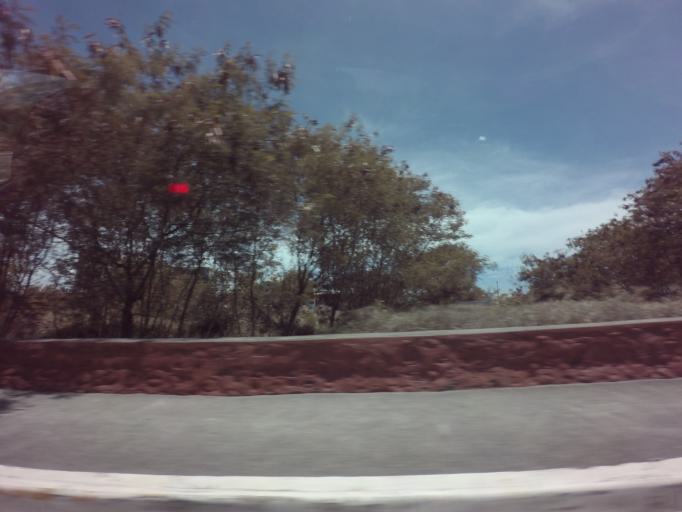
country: PH
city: Sambayanihan People's Village
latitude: 14.4916
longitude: 120.9964
